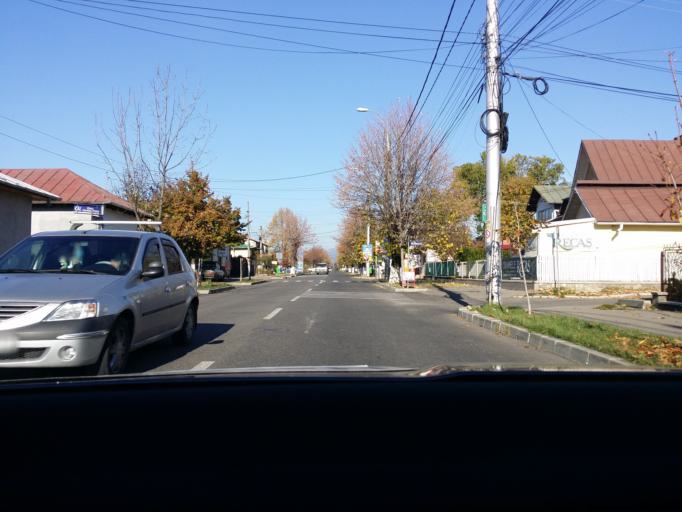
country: RO
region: Prahova
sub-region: Municipiul Campina
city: Campina
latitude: 45.1376
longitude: 25.7260
